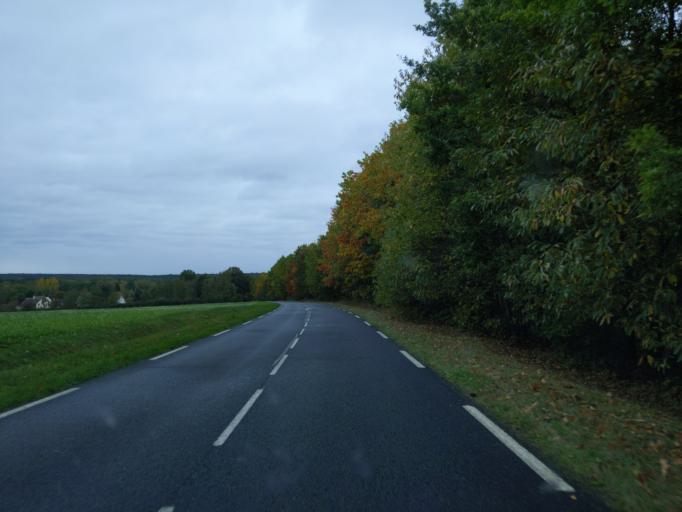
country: FR
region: Ile-de-France
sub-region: Departement des Yvelines
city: Bullion
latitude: 48.6324
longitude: 1.9970
